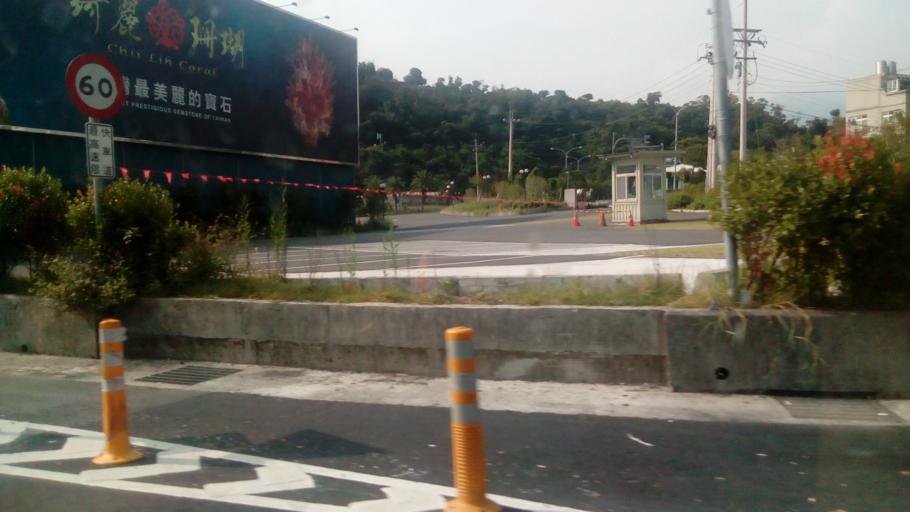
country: TW
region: Taiwan
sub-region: Yilan
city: Yilan
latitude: 24.5963
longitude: 121.8567
